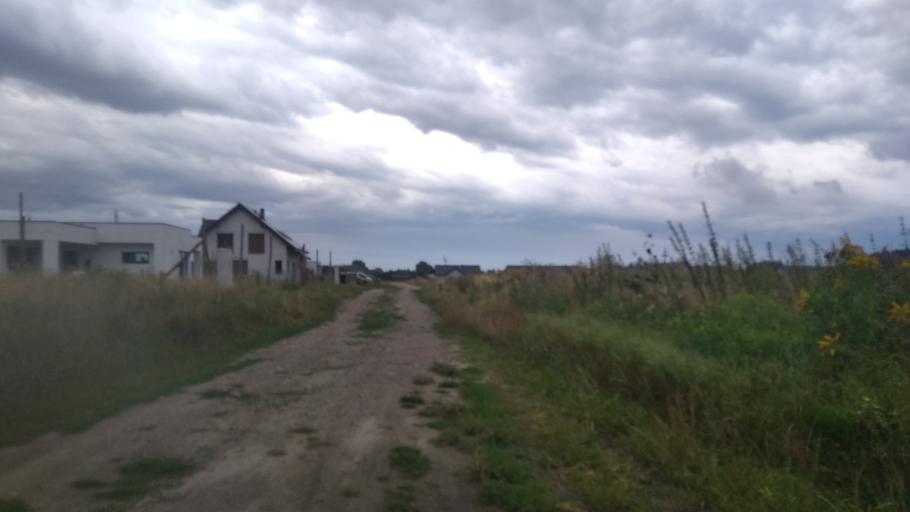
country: PL
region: Kujawsko-Pomorskie
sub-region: Powiat bydgoski
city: Osielsko
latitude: 53.2176
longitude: 18.1337
